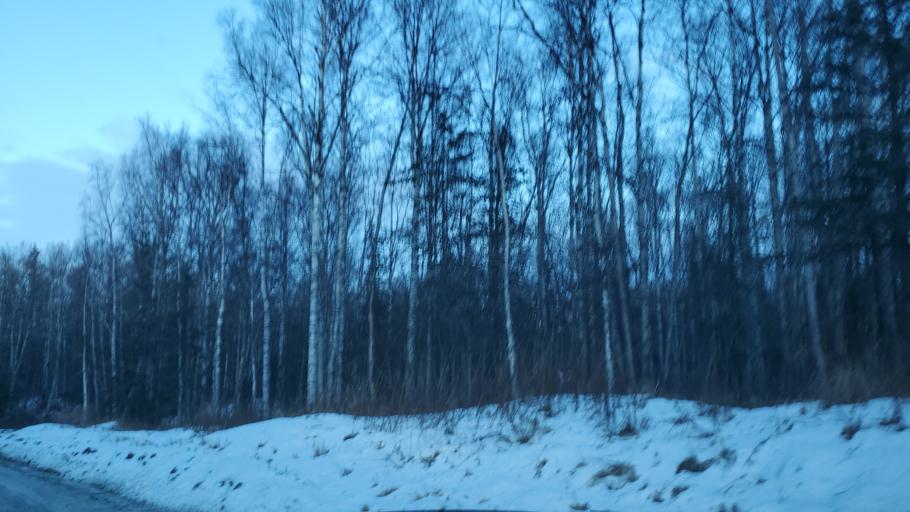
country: US
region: Alaska
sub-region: Matanuska-Susitna Borough
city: Lakes
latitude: 61.6625
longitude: -149.3275
